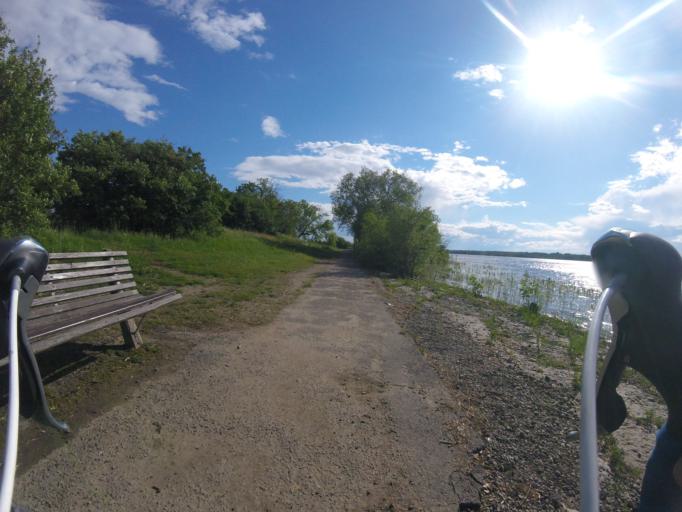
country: CA
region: Ontario
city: Ottawa
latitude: 45.4012
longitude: -75.7594
